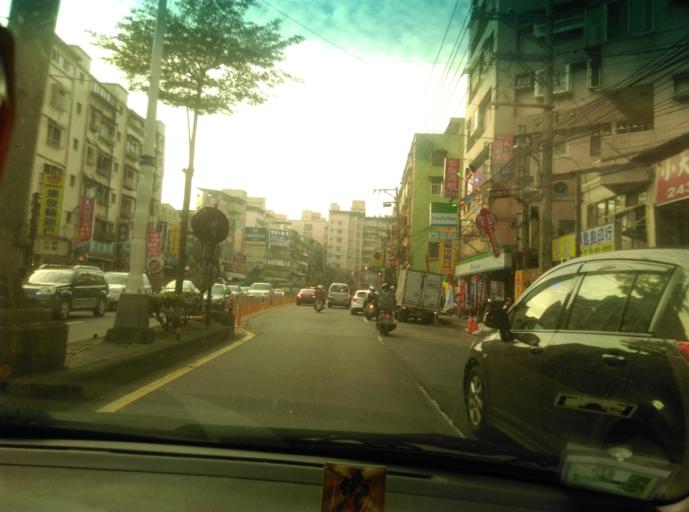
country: TW
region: Taiwan
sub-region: Keelung
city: Keelung
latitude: 25.1403
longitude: 121.7121
